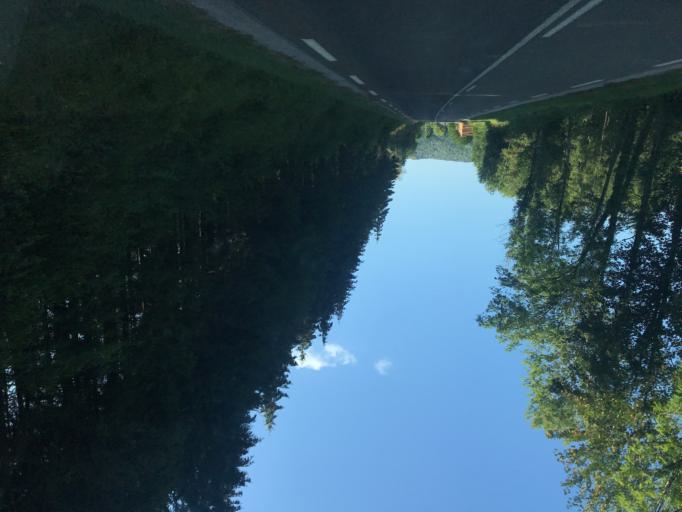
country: FR
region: Franche-Comte
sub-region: Departement du Jura
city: Moirans-en-Montagne
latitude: 46.4046
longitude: 5.7341
